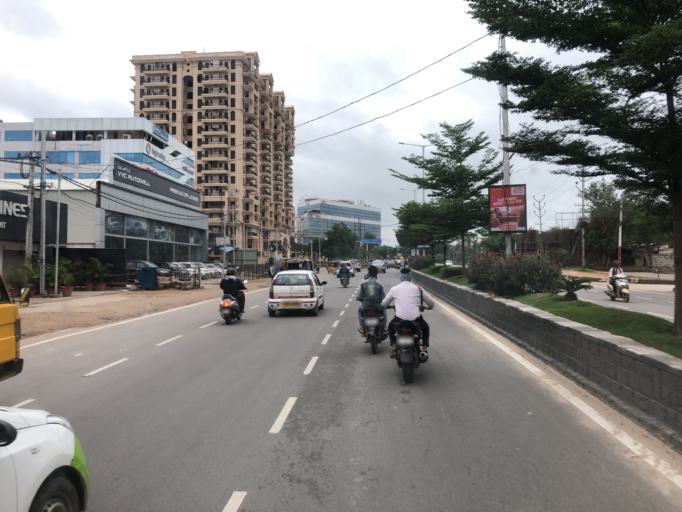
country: IN
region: Telangana
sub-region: Rangareddi
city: Kukatpalli
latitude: 17.4570
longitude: 78.3650
